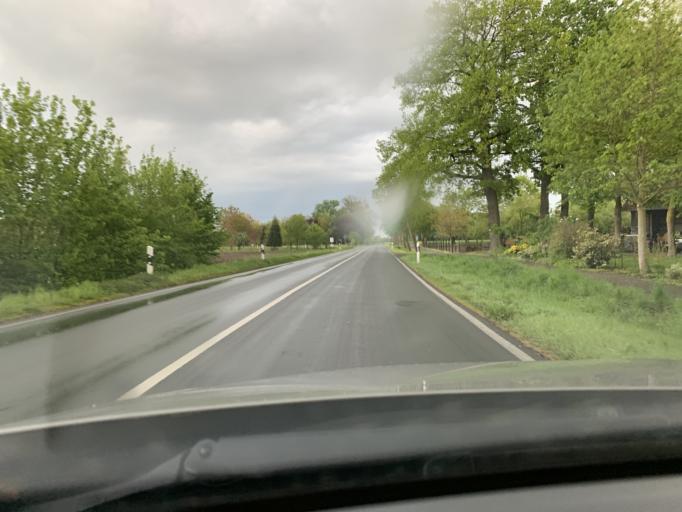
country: DE
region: North Rhine-Westphalia
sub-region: Regierungsbezirk Detmold
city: Langenberg
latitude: 51.7911
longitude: 8.3714
